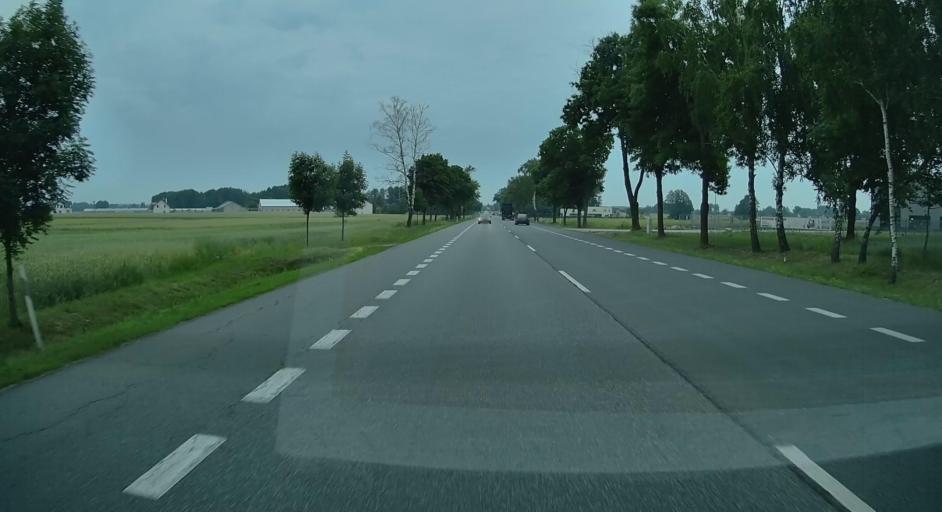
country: PL
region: Masovian Voivodeship
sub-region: Powiat siedlecki
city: Zbuczyn
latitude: 52.0950
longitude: 22.4182
